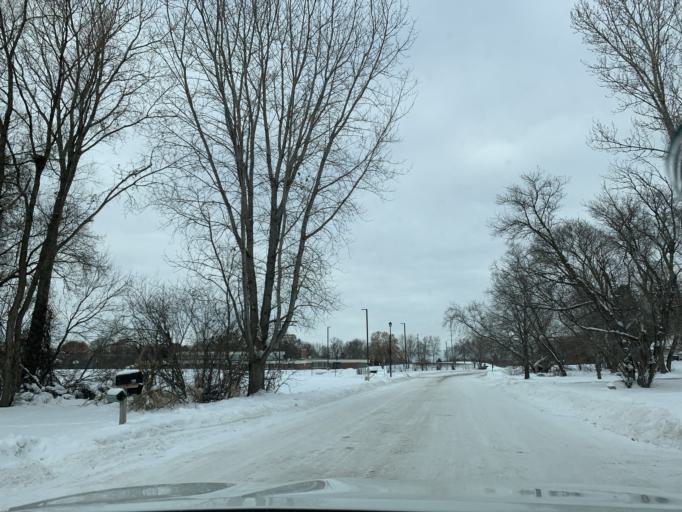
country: US
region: Minnesota
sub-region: Anoka County
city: Coon Rapids
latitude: 45.1699
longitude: -93.2989
